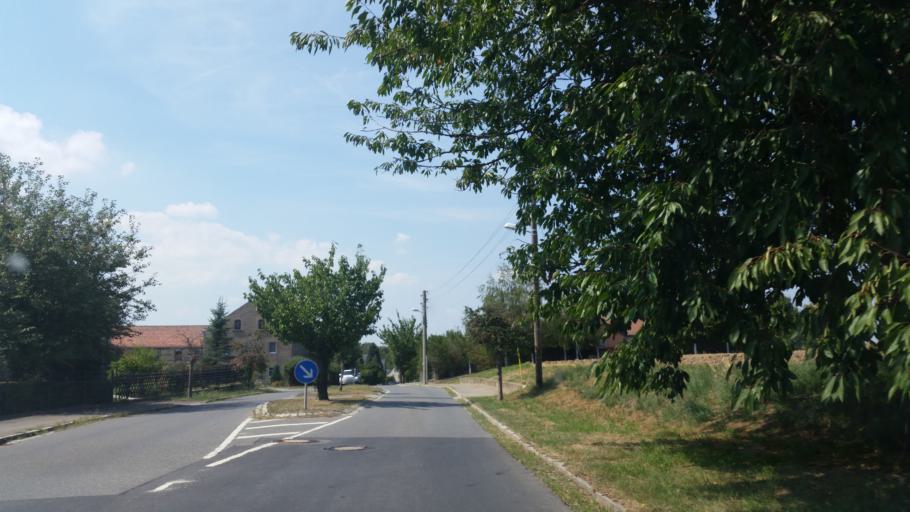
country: DE
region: Saxony
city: Wilsdruff
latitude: 51.0678
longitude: 13.5432
